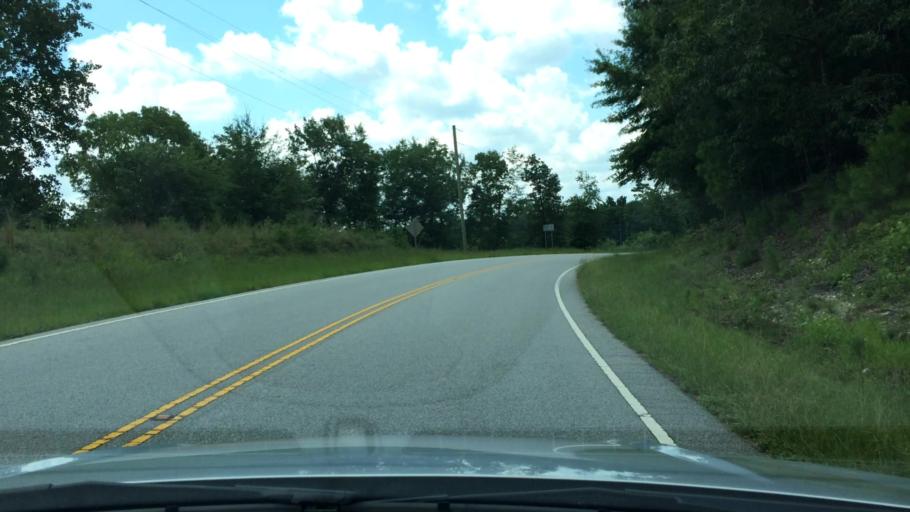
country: US
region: South Carolina
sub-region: Calhoun County
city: Oak Grove
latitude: 33.8092
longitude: -81.0087
